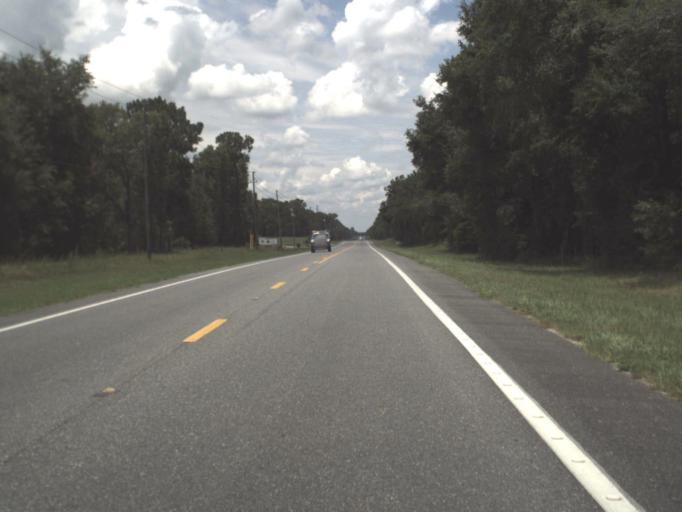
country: US
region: Florida
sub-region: Levy County
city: Williston Highlands
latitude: 29.3402
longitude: -82.5127
